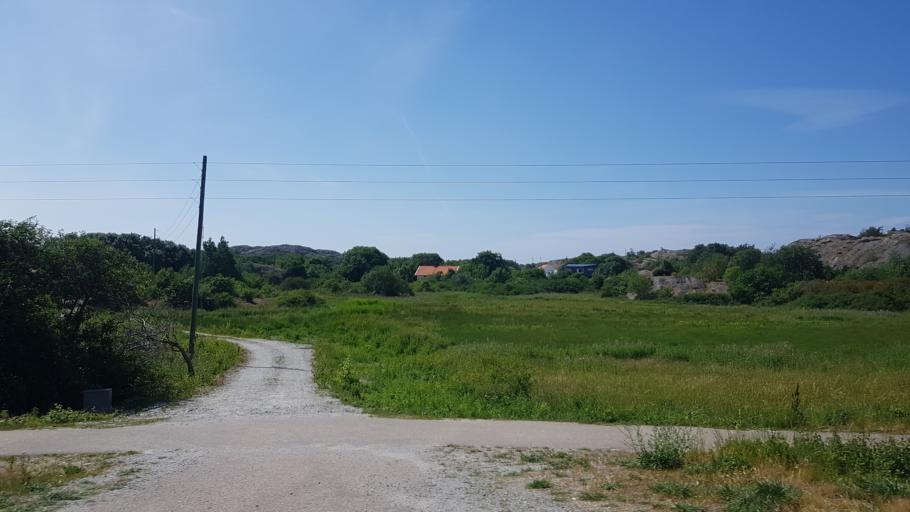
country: SE
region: Vaestra Goetaland
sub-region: Tjorns Kommun
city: Skaerhamn
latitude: 57.9650
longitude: 11.5587
